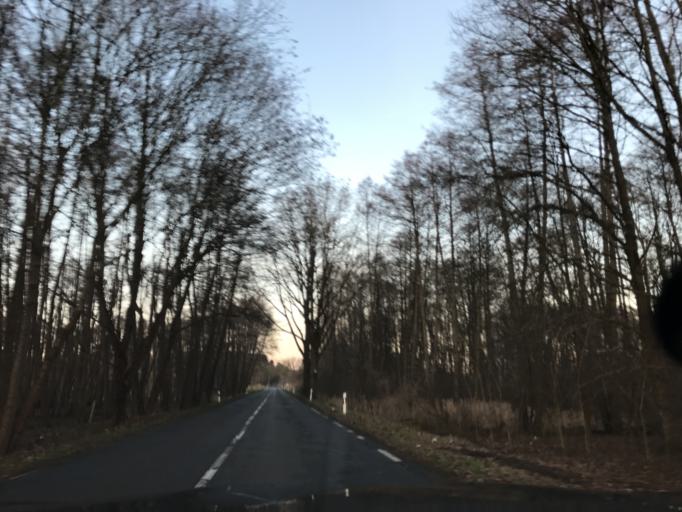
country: DE
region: Brandenburg
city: Wusterwitz
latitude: 52.4448
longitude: 12.4328
